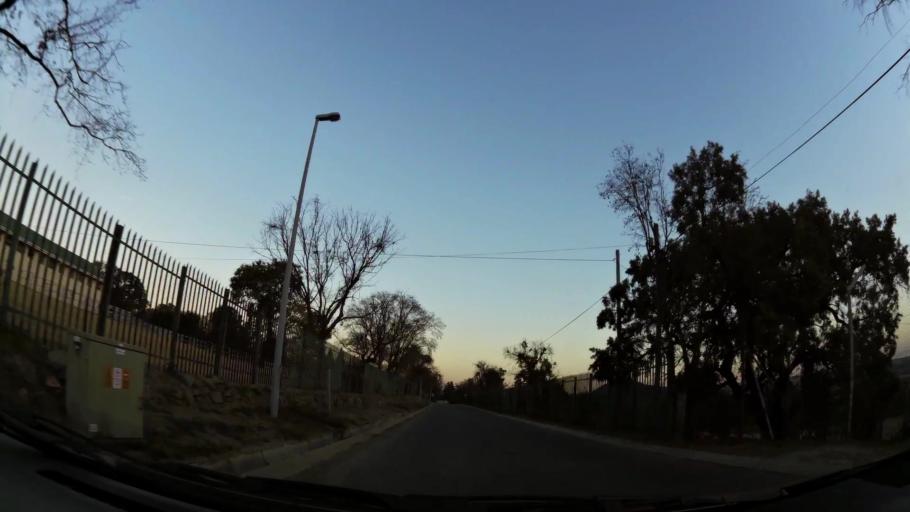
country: ZA
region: Gauteng
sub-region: City of Johannesburg Metropolitan Municipality
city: Midrand
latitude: -26.0082
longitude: 28.0527
